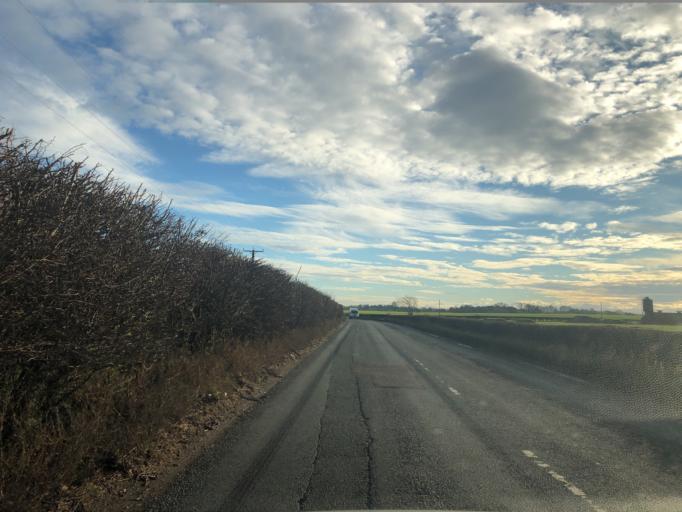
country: GB
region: England
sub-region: North Yorkshire
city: Thirsk
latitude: 54.1761
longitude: -1.3689
